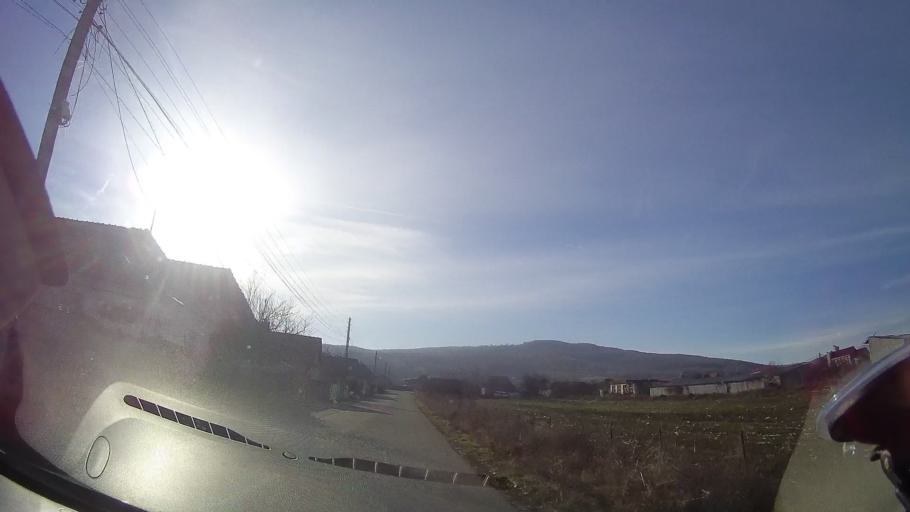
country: RO
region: Bihor
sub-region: Comuna Magesti
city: Magesti
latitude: 47.0100
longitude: 22.4524
